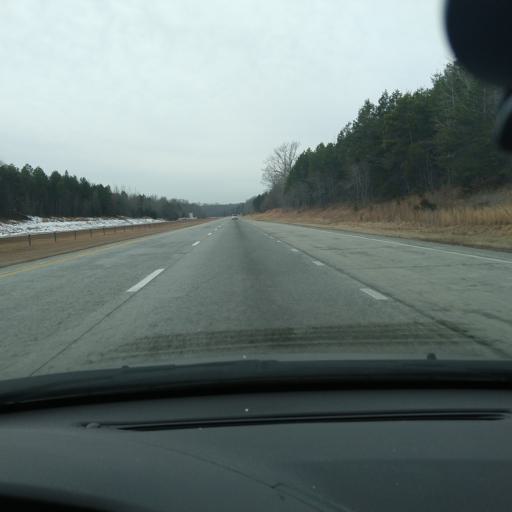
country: US
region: North Carolina
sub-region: Davidson County
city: Welcome
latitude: 35.8729
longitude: -80.2506
